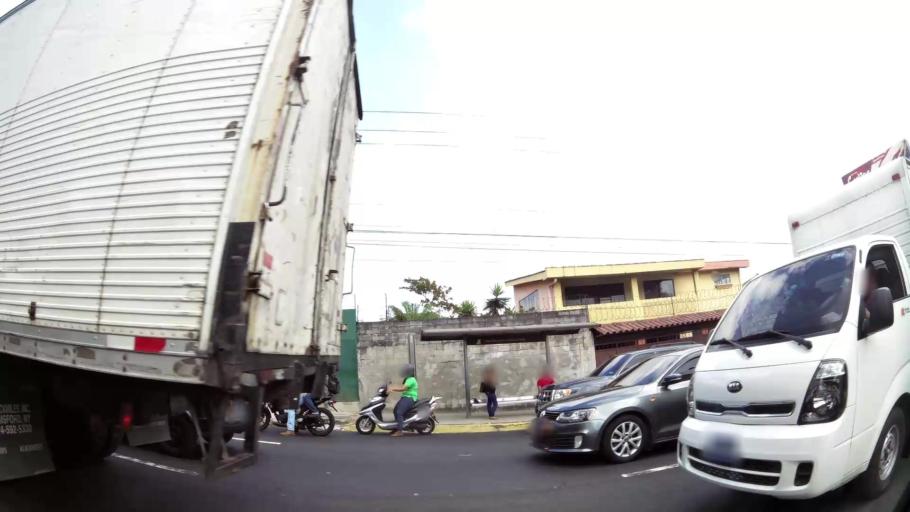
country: SV
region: San Salvador
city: Mejicanos
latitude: 13.7100
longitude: -89.2311
